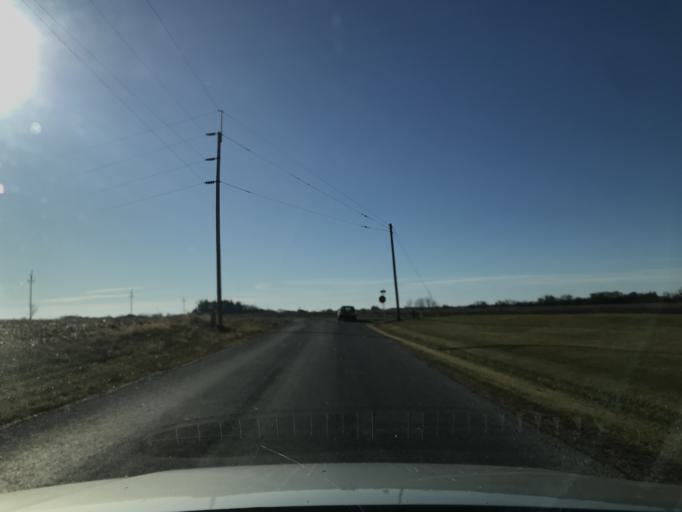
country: US
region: Illinois
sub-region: Hancock County
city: Carthage
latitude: 40.4619
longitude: -91.1784
